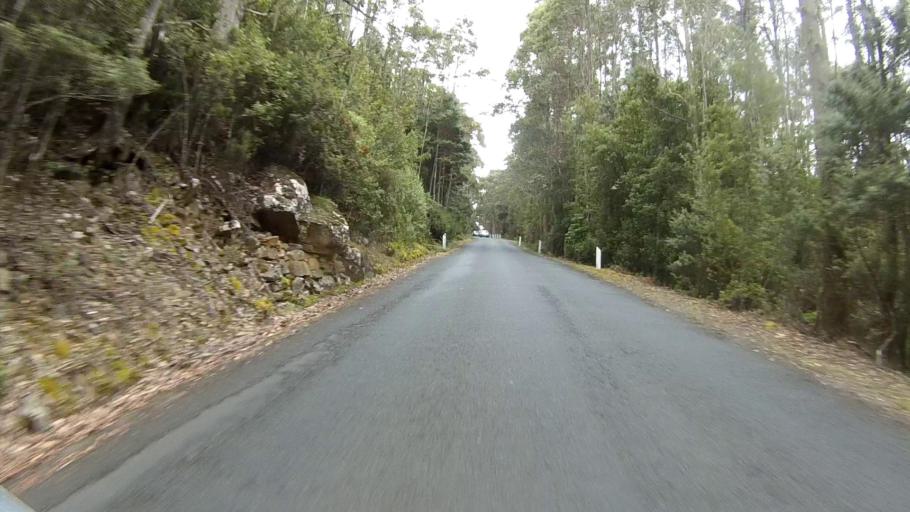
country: AU
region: Tasmania
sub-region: Glenorchy
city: West Moonah
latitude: -42.9065
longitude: 147.2442
